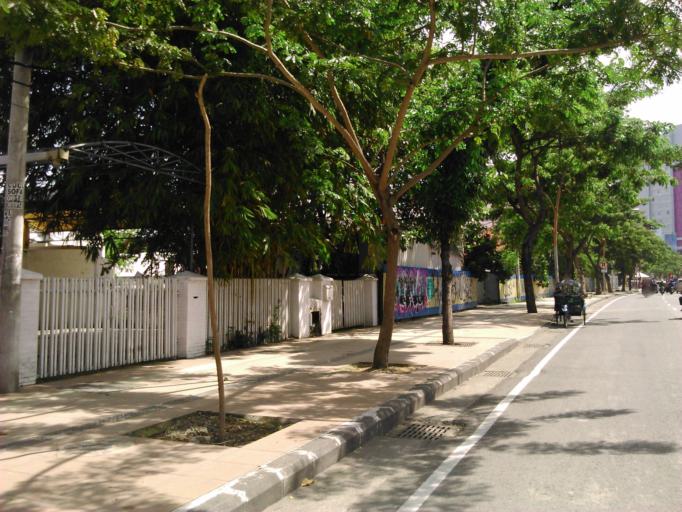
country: ID
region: East Java
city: Gubengairlangga
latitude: -7.2755
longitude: 112.7464
